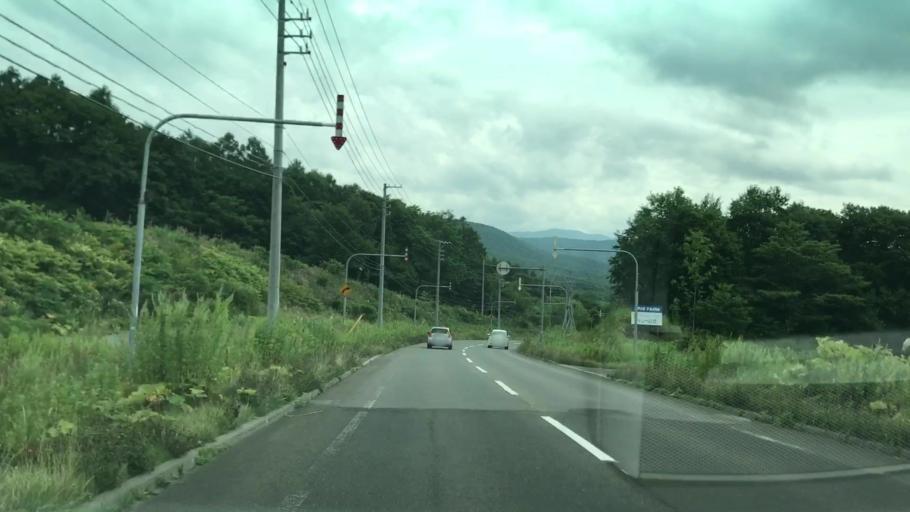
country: JP
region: Hokkaido
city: Yoichi
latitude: 43.1085
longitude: 140.8215
